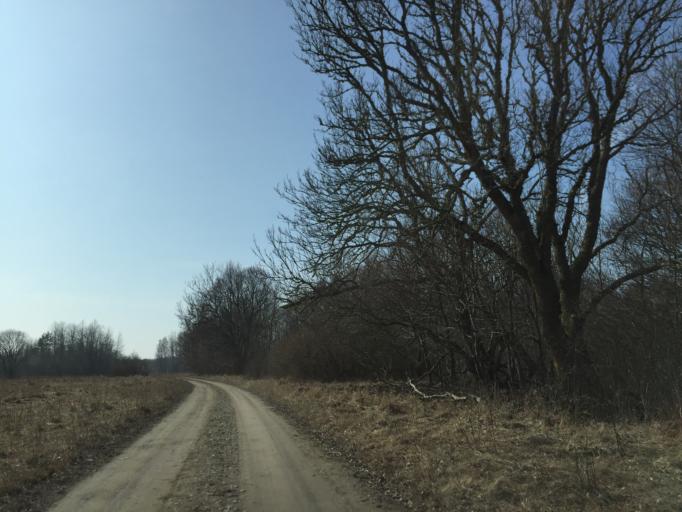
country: LV
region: Dundaga
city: Dundaga
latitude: 57.9336
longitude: 22.0655
